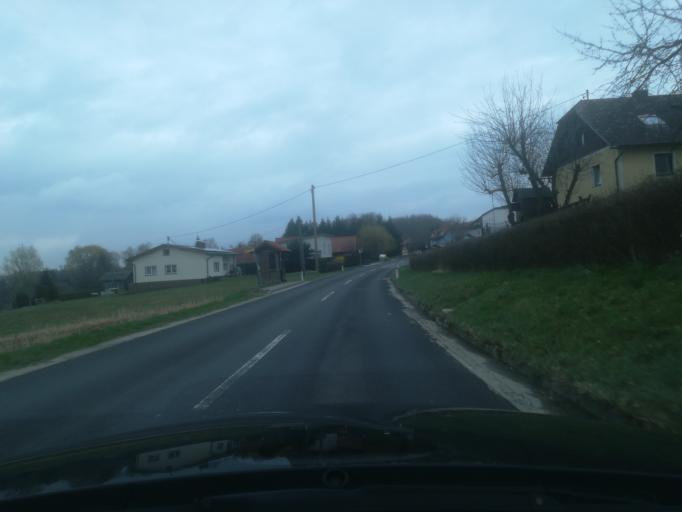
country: AT
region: Upper Austria
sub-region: Politischer Bezirk Urfahr-Umgebung
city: Feldkirchen an der Donau
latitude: 48.3219
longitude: 13.9838
